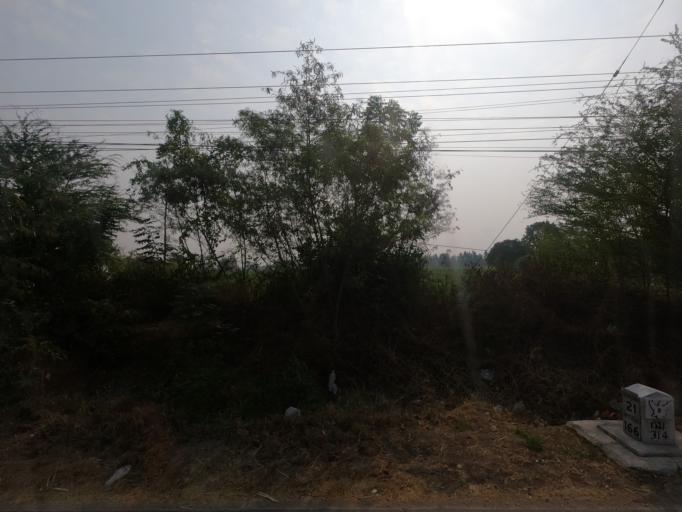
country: TH
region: Khon Kaen
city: Ban Haet
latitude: 16.2351
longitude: 102.7683
